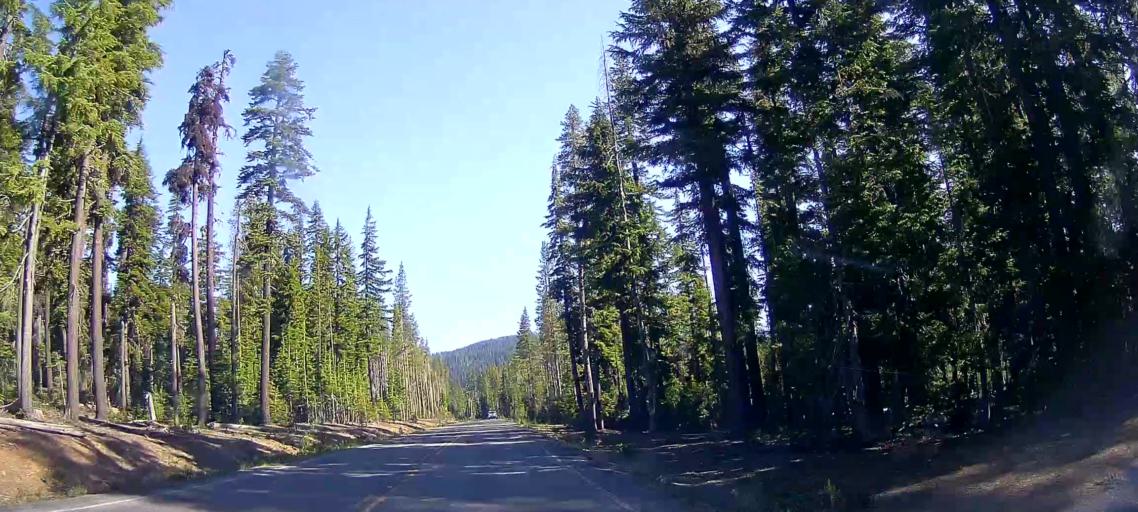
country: US
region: Oregon
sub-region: Jackson County
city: Shady Cove
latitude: 42.8551
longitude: -122.1530
